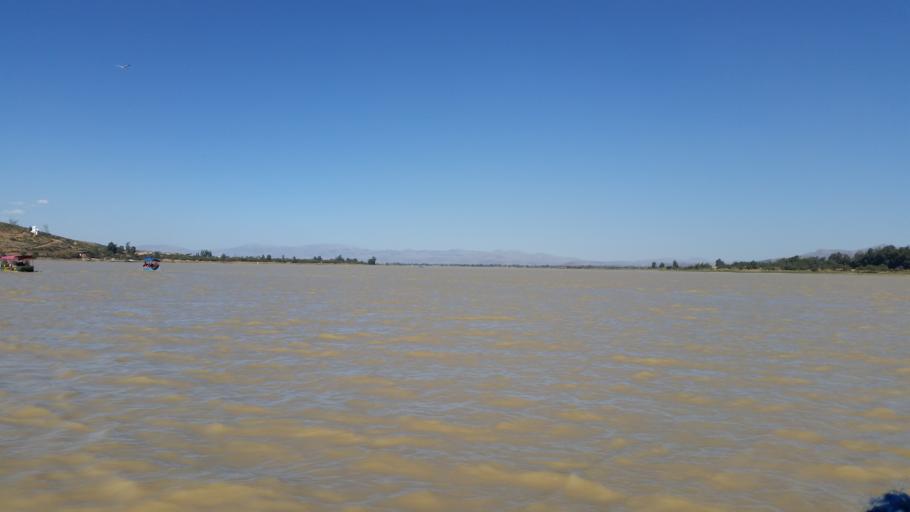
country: BO
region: Cochabamba
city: Tarata
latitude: -17.5342
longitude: -66.0946
